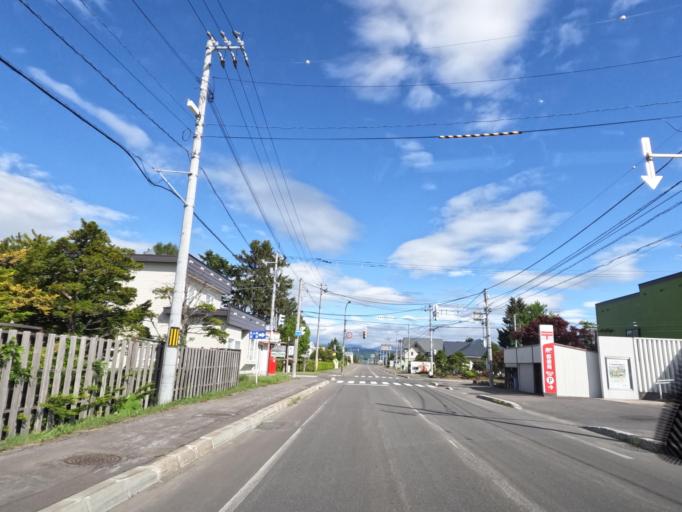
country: JP
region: Hokkaido
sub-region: Asahikawa-shi
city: Asahikawa
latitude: 43.7178
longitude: 142.5281
